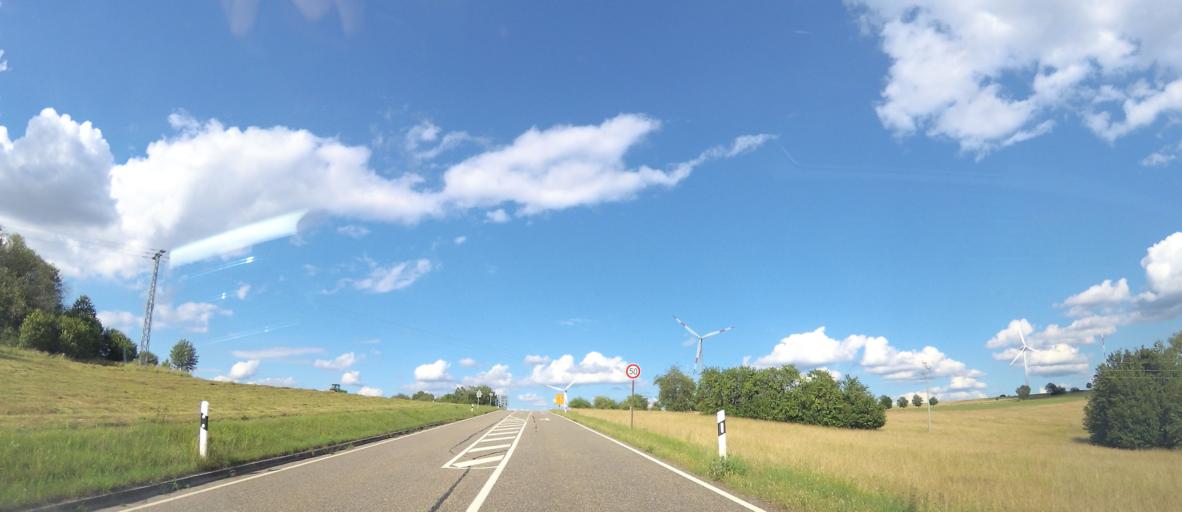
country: DE
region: Rheinland-Pfalz
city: Vinningen
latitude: 49.1513
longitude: 7.5652
